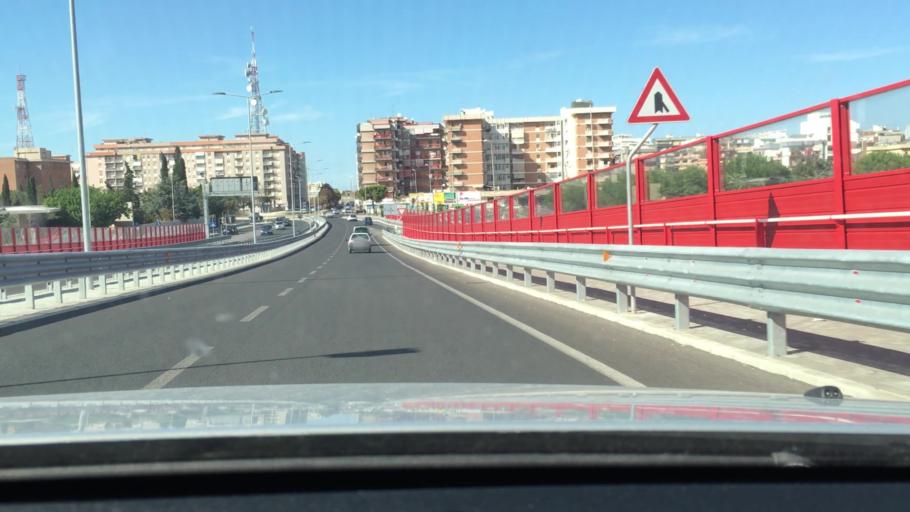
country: IT
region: Apulia
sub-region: Provincia di Bari
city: Bari
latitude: 41.1231
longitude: 16.8481
